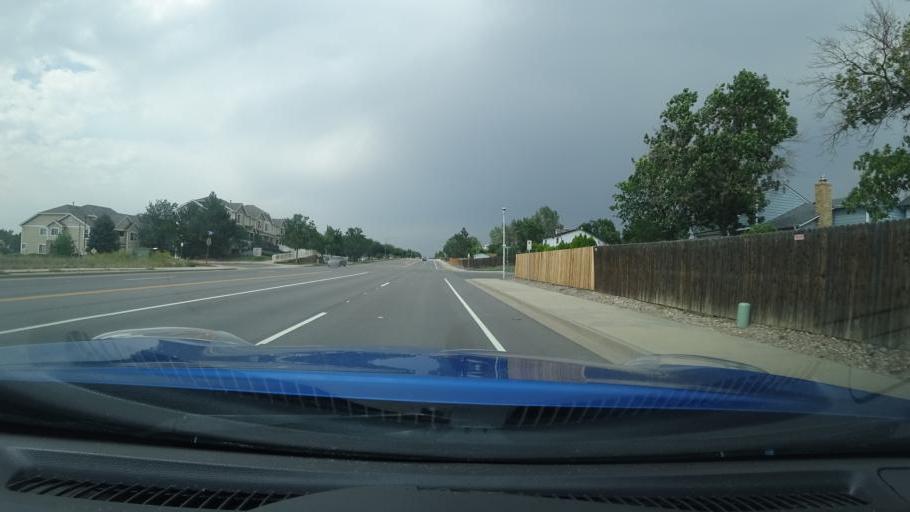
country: US
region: Colorado
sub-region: Adams County
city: Aurora
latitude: 39.6866
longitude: -104.7629
